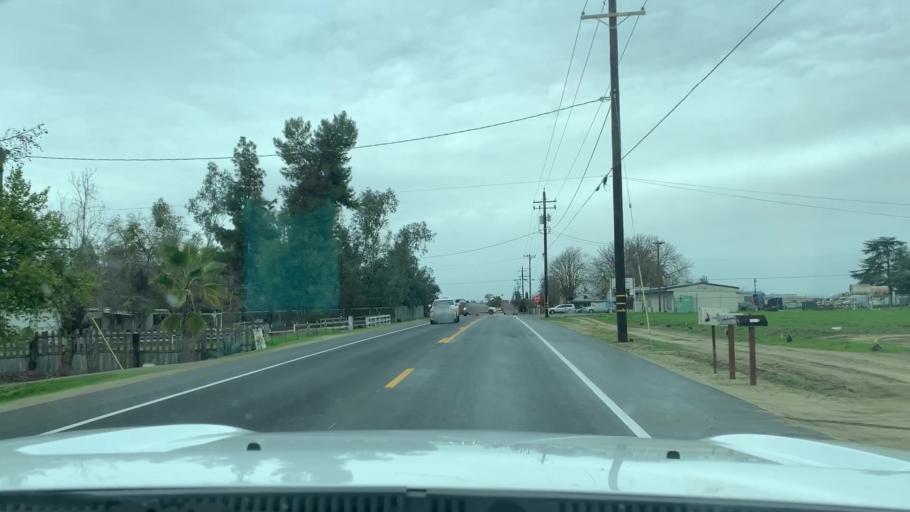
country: US
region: California
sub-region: Fresno County
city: Fowler
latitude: 36.5752
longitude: -119.6825
